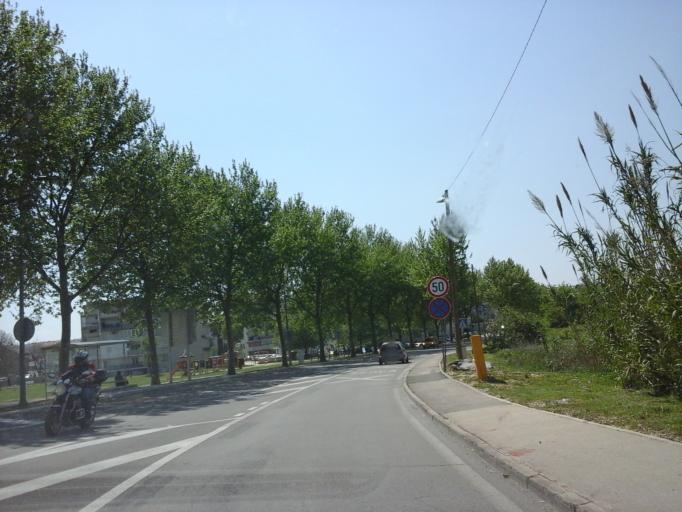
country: HR
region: Splitsko-Dalmatinska
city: Solin
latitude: 43.5411
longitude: 16.4915
